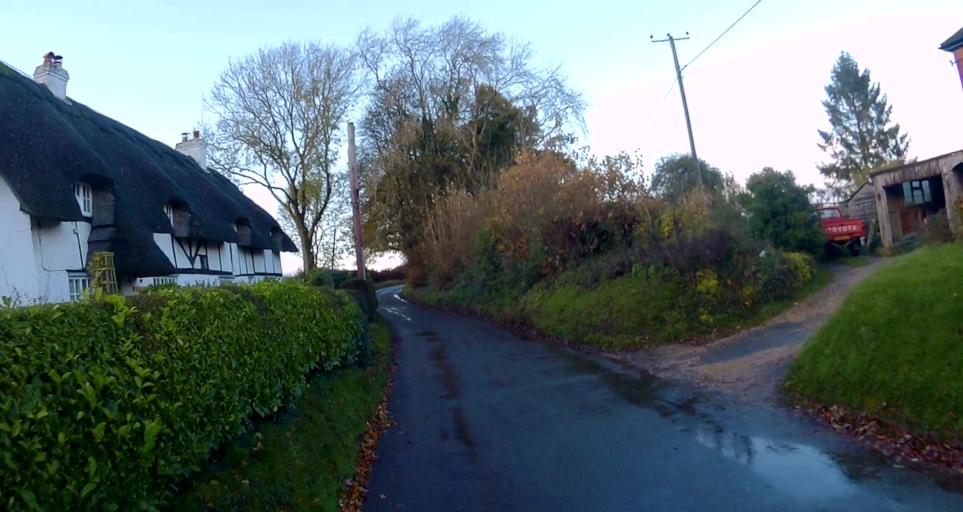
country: GB
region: England
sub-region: Hampshire
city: Basingstoke
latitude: 51.2118
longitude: -1.0898
